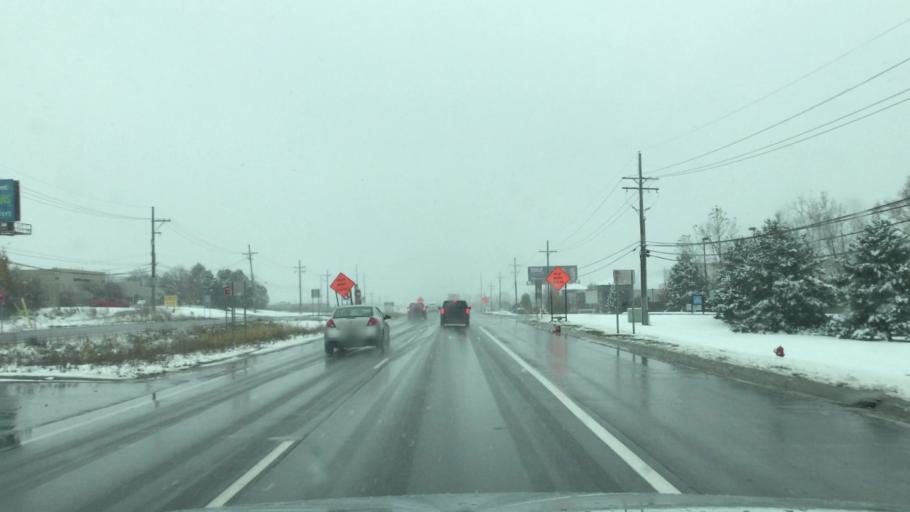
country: US
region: Michigan
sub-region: Oakland County
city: Auburn Hills
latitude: 42.7167
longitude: -83.2428
